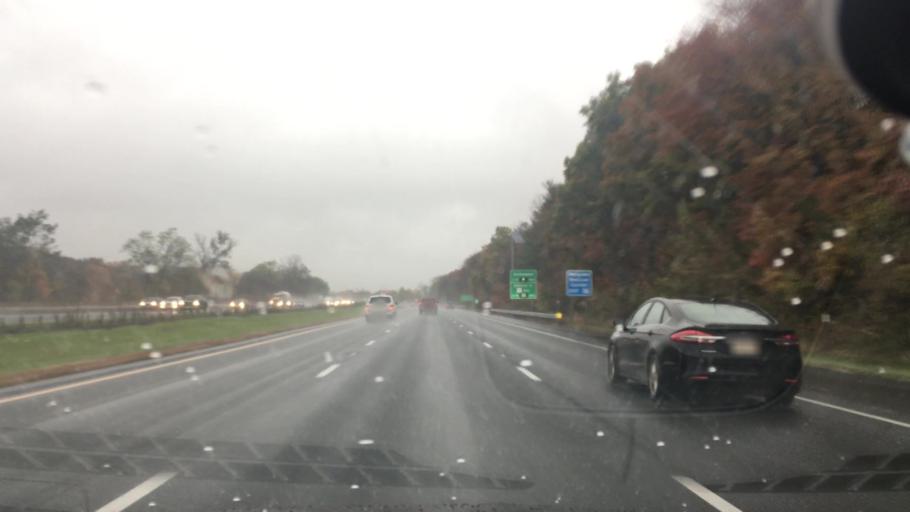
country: US
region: Massachusetts
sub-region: Hampden County
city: Holyoke
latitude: 42.1839
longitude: -72.6402
